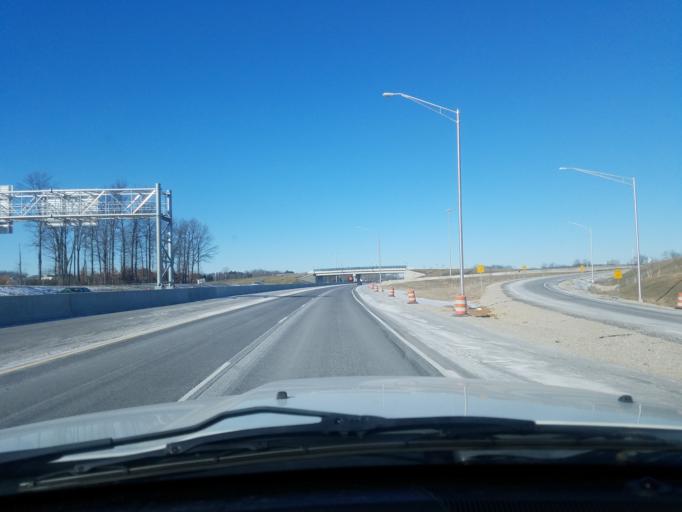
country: US
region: Indiana
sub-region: Monroe County
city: Bloomington
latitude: 39.1197
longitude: -86.5691
